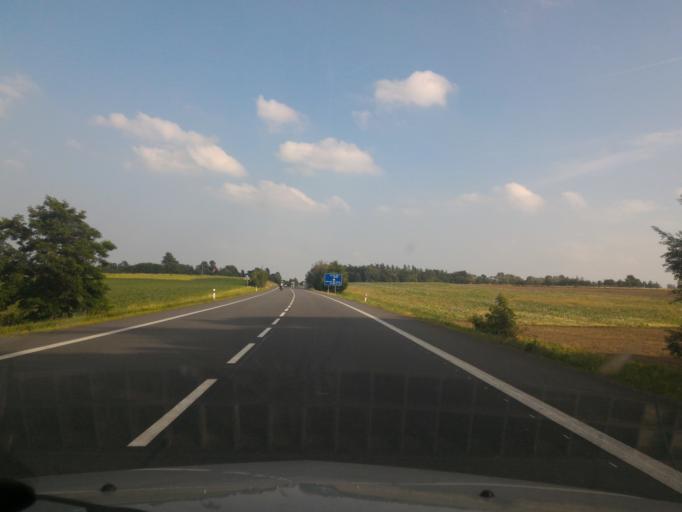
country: CZ
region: Vysocina
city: Golcuv Jenikov
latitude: 49.8153
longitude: 15.4665
